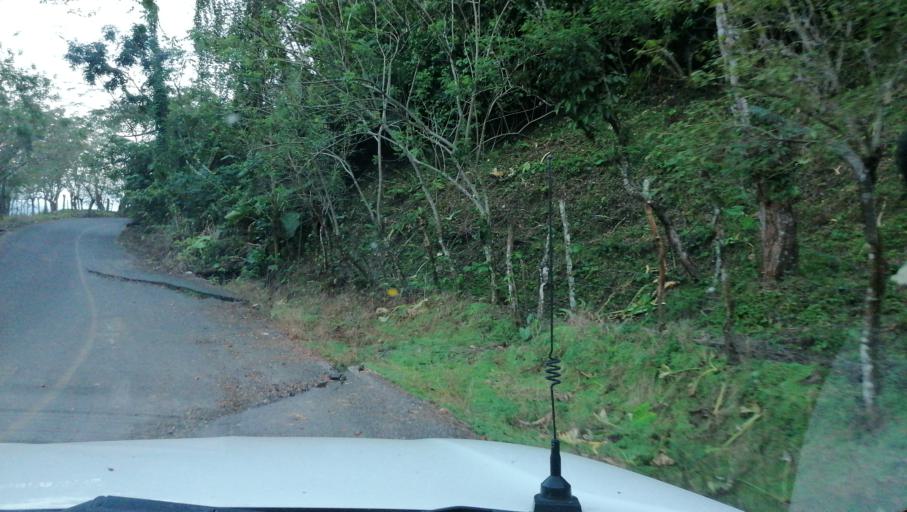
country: MX
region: Chiapas
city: Ostuacan
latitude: 17.4244
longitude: -93.3417
